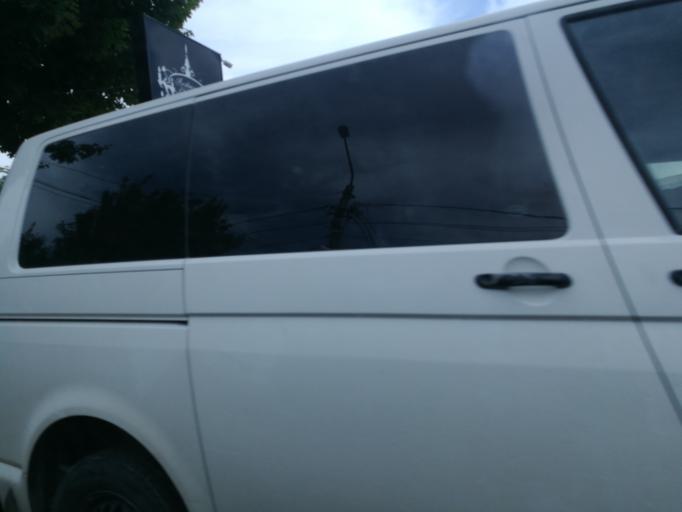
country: RO
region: Constanta
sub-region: Oras Eforie
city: Eforie Nord
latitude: 44.0648
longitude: 28.6341
